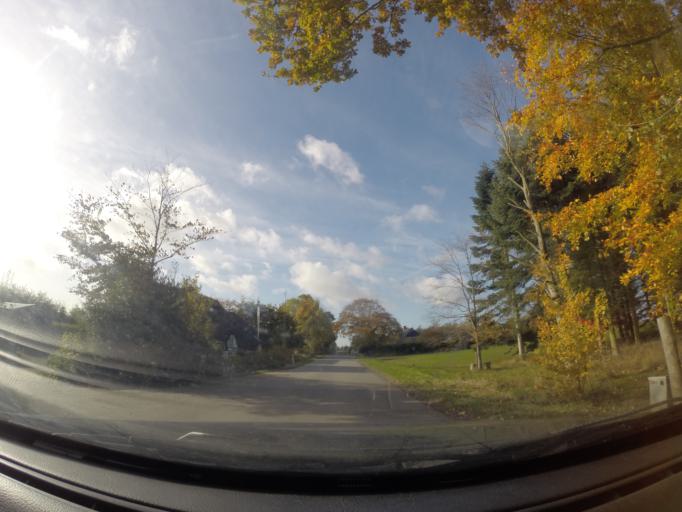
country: DK
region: South Denmark
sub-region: Svendborg Kommune
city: Svendborg
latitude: 55.0568
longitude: 10.4932
